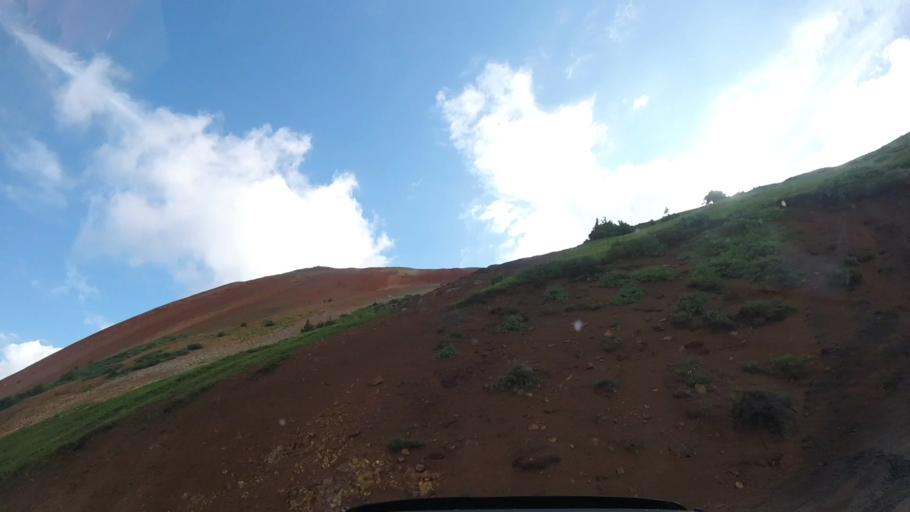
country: US
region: Colorado
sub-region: San Juan County
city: Silverton
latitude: 37.9079
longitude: -107.6635
